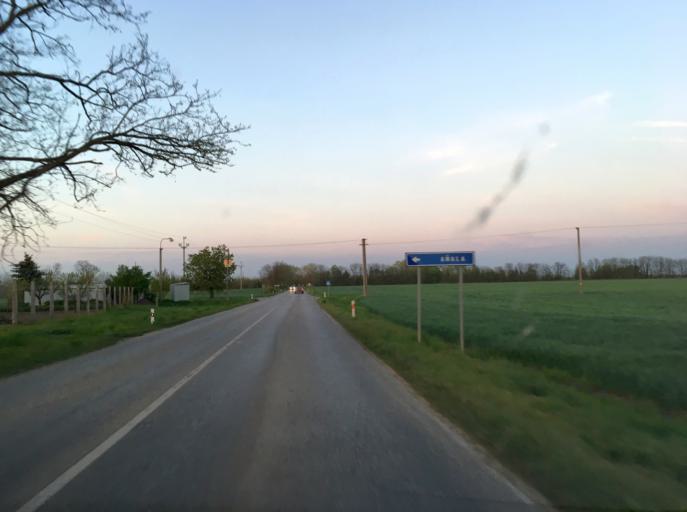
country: SK
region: Nitriansky
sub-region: Okres Nove Zamky
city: Nove Zamky
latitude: 47.9554
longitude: 18.1414
